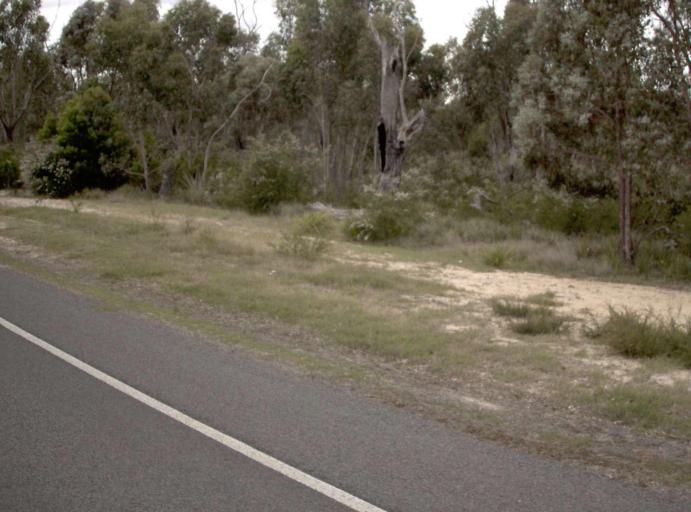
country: AU
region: Victoria
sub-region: Wellington
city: Sale
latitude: -38.3242
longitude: 147.0196
